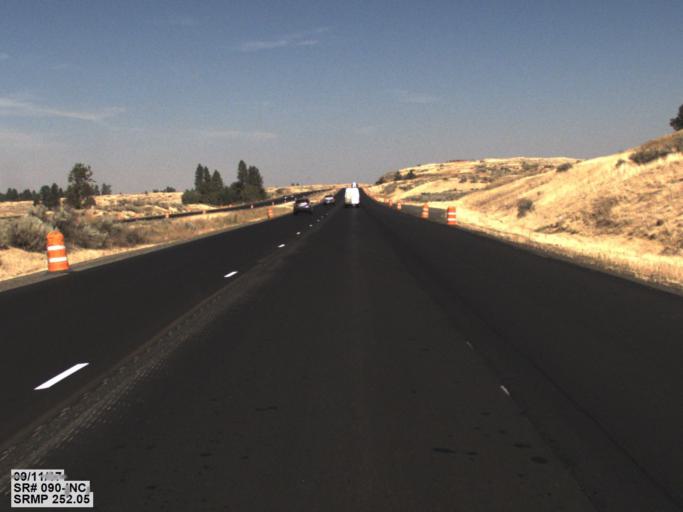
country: US
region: Washington
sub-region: Spokane County
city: Medical Lake
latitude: 47.3759
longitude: -117.8717
